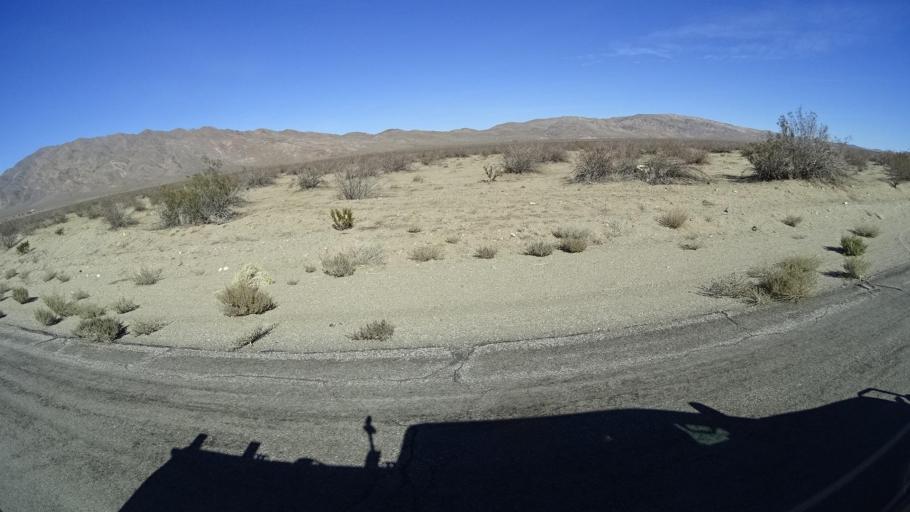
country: US
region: California
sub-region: Kern County
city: China Lake Acres
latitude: 35.3892
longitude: -117.7665
